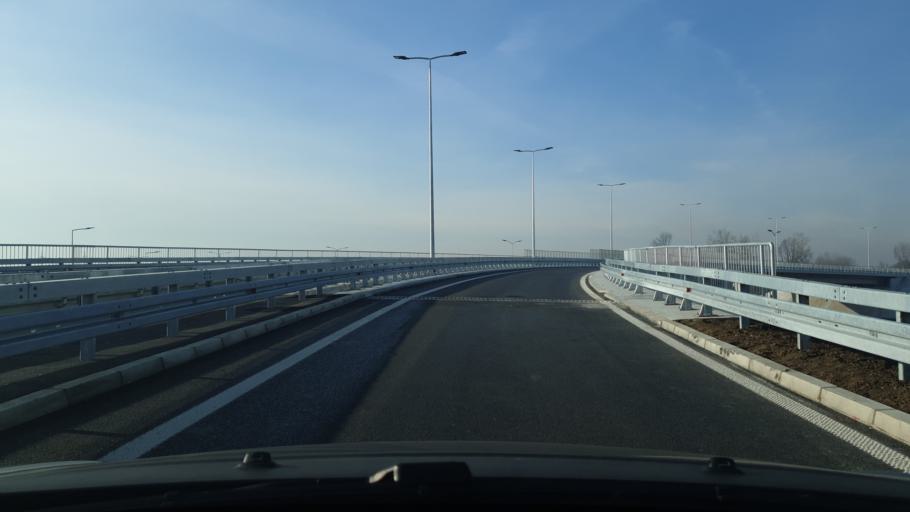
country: RS
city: Baric
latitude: 44.6515
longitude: 20.2325
